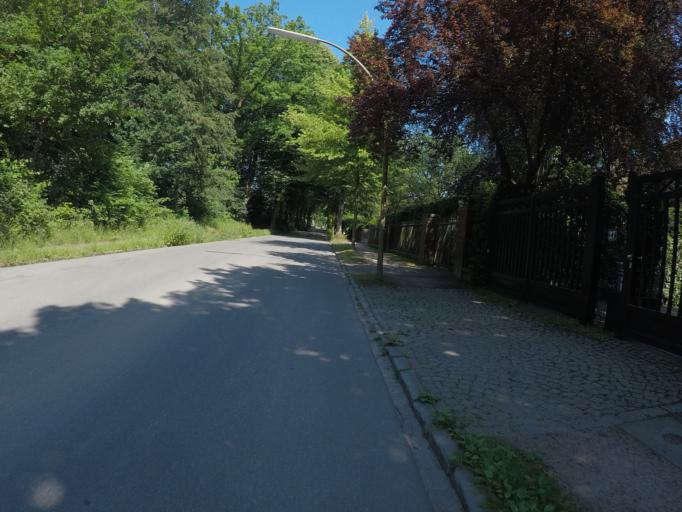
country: DE
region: Hamburg
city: Bergstedt
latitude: 53.6454
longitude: 10.1538
